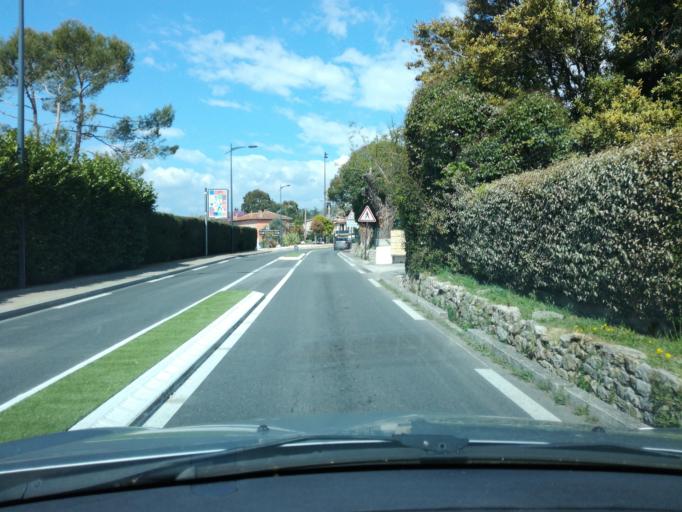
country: FR
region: Provence-Alpes-Cote d'Azur
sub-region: Departement des Alpes-Maritimes
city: Mougins
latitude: 43.6042
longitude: 7.0094
